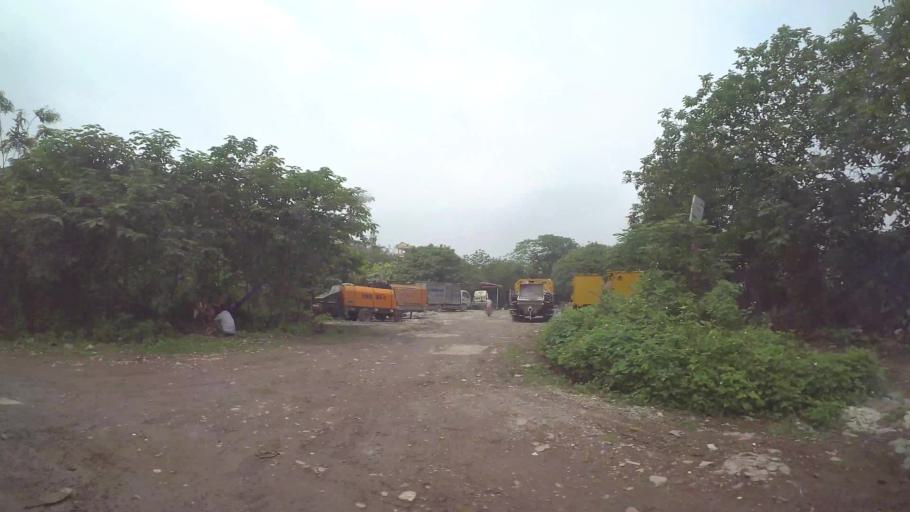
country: VN
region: Ha Noi
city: Van Dien
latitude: 20.9693
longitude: 105.8462
